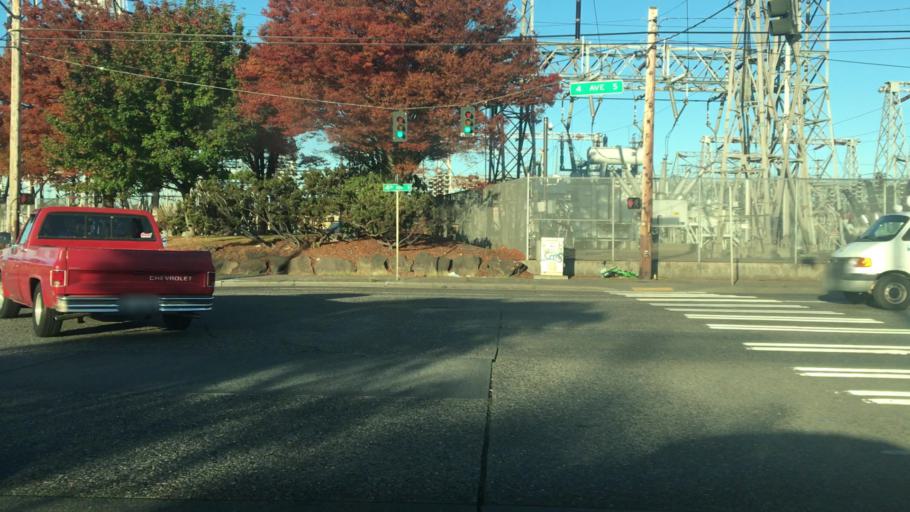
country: US
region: Washington
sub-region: King County
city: Seattle
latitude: 47.5677
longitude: -122.3290
